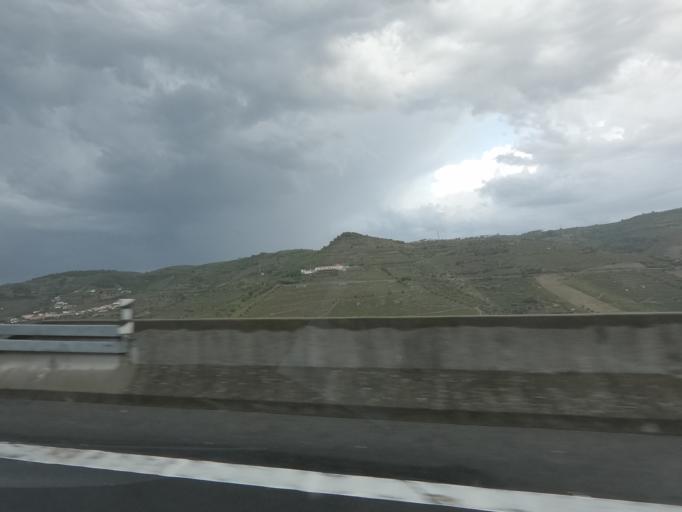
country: PT
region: Vila Real
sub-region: Peso da Regua
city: Peso da Regua
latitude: 41.1858
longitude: -7.7489
